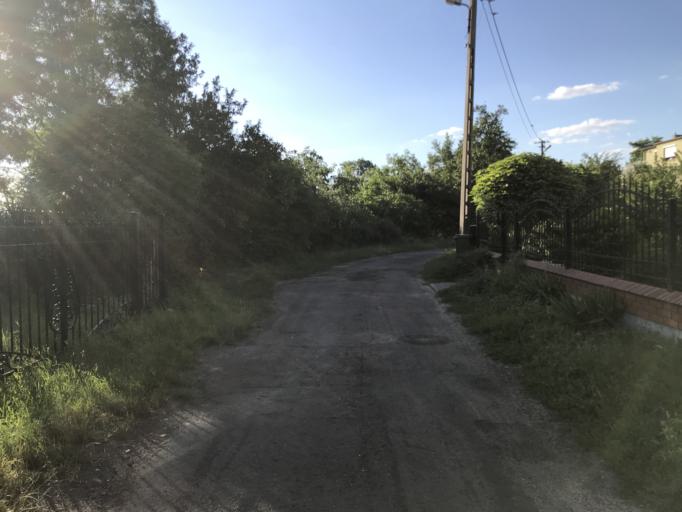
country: PL
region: Greater Poland Voivodeship
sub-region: Kalisz
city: Kalisz
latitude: 51.7671
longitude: 18.1000
